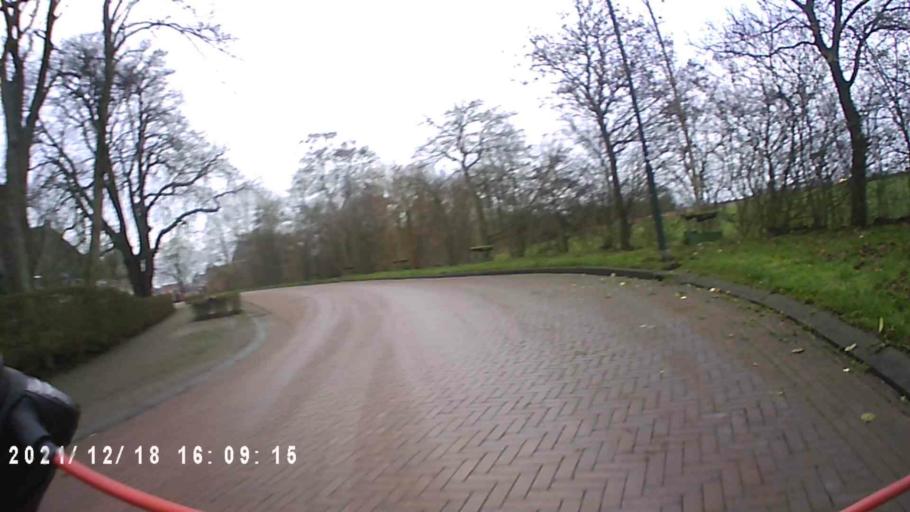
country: NL
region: Friesland
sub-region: Gemeente Dongeradeel
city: Anjum
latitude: 53.3602
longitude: 6.0718
